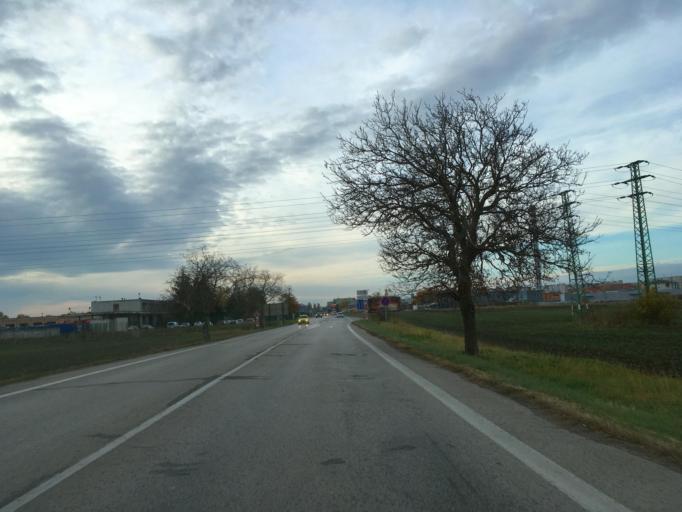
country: SK
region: Trnavsky
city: Dunajska Streda
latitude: 47.9855
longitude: 17.6377
